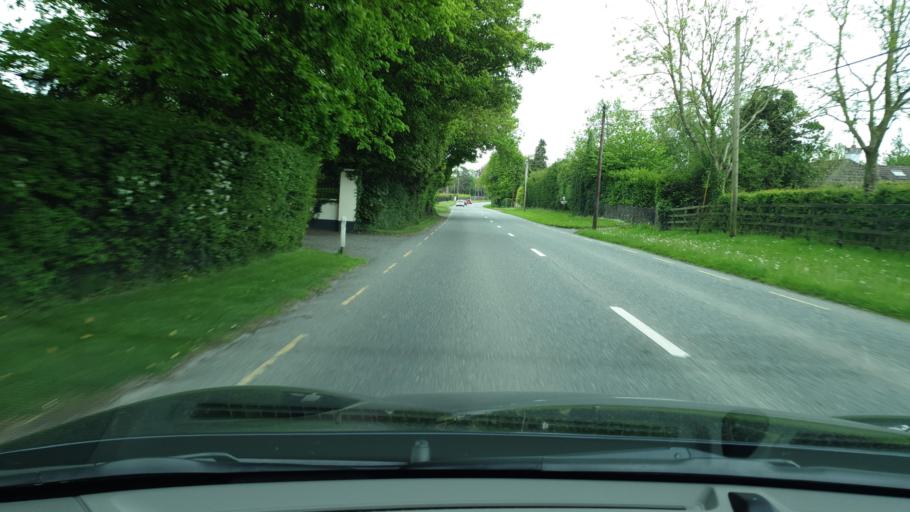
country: IE
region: Leinster
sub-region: An Mhi
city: Dunboyne
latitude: 53.4540
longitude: -6.4938
